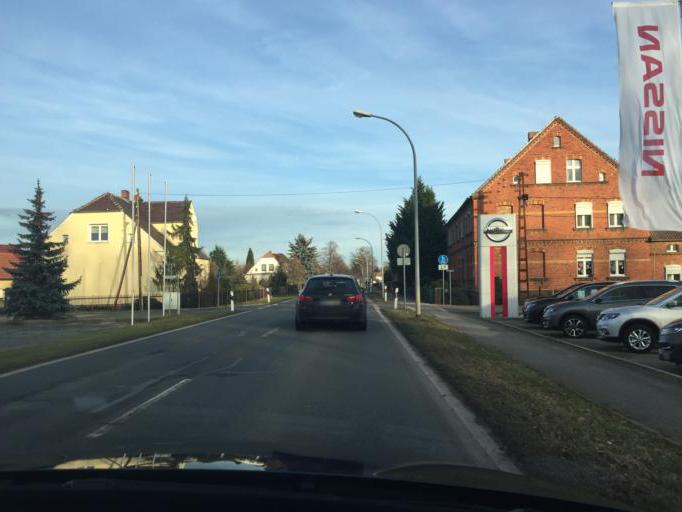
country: DE
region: Brandenburg
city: Forst
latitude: 51.7239
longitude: 14.6115
